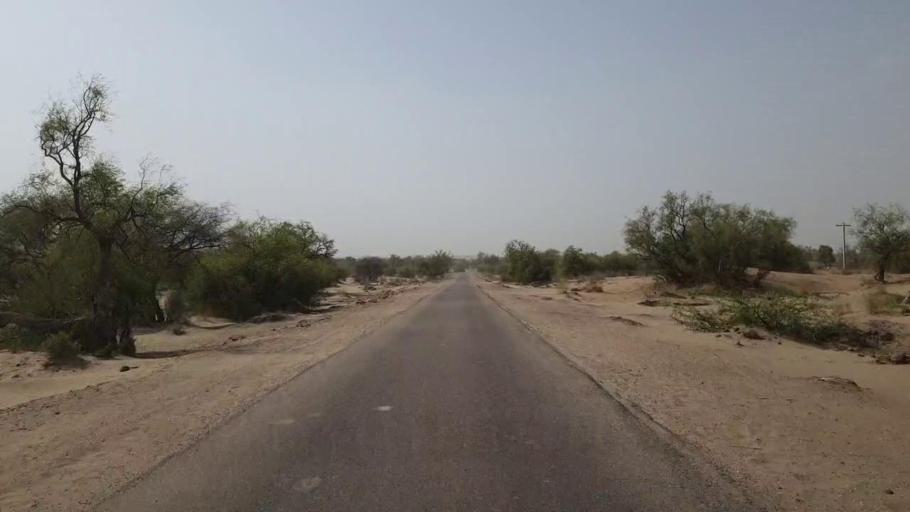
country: PK
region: Sindh
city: Mithi
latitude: 24.6063
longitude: 69.9214
